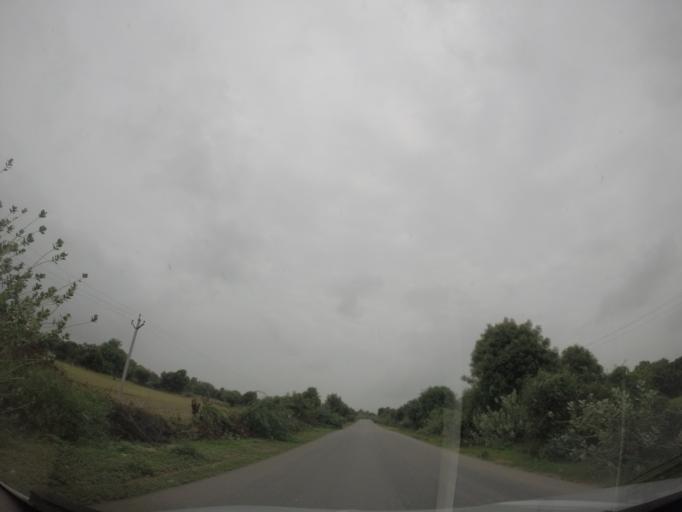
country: IN
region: Rajasthan
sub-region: Jalore
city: Sanchor
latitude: 24.6761
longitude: 71.8381
